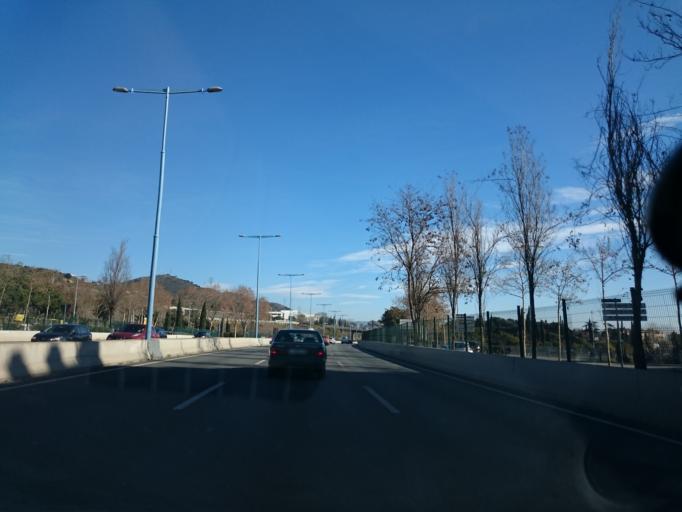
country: ES
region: Catalonia
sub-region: Provincia de Barcelona
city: Horta-Guinardo
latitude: 41.4368
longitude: 2.1498
